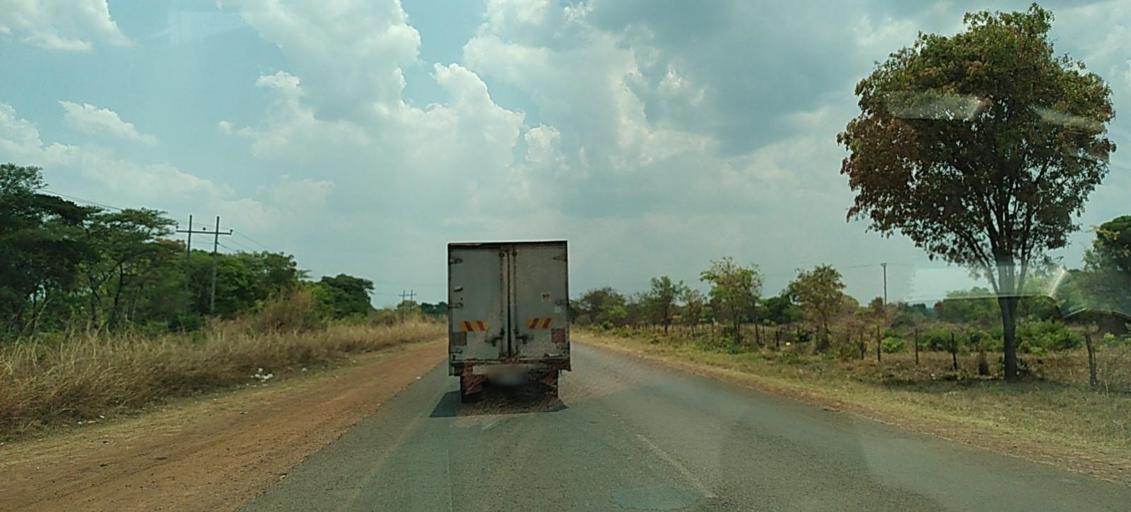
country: ZM
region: Copperbelt
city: Kalulushi
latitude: -12.8358
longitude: 27.9519
